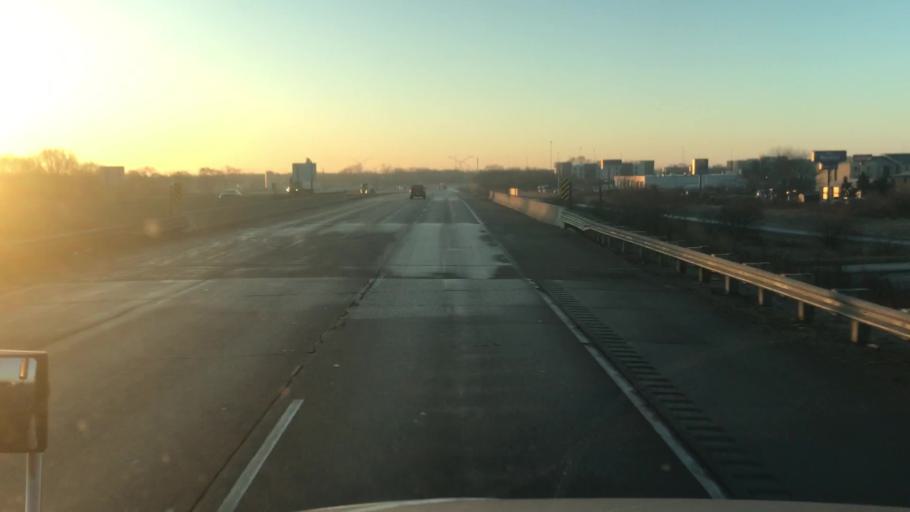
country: US
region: Iowa
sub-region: Black Hawk County
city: Waterloo
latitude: 42.4692
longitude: -92.3192
